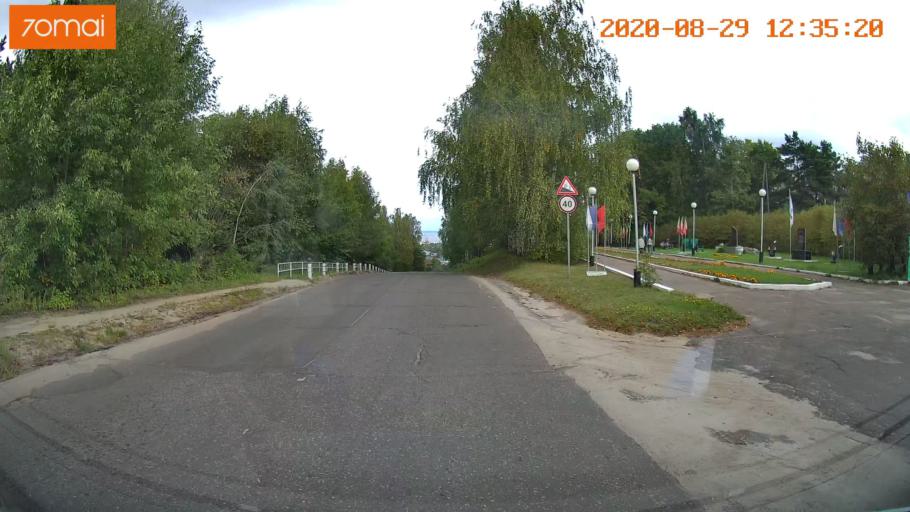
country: RU
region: Ivanovo
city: Yur'yevets
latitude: 57.3131
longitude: 43.1068
